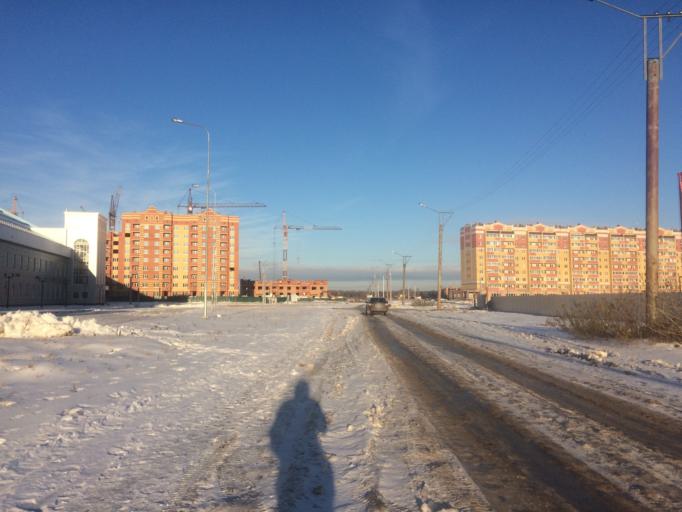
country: RU
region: Mariy-El
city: Yoshkar-Ola
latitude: 56.6390
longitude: 47.9174
